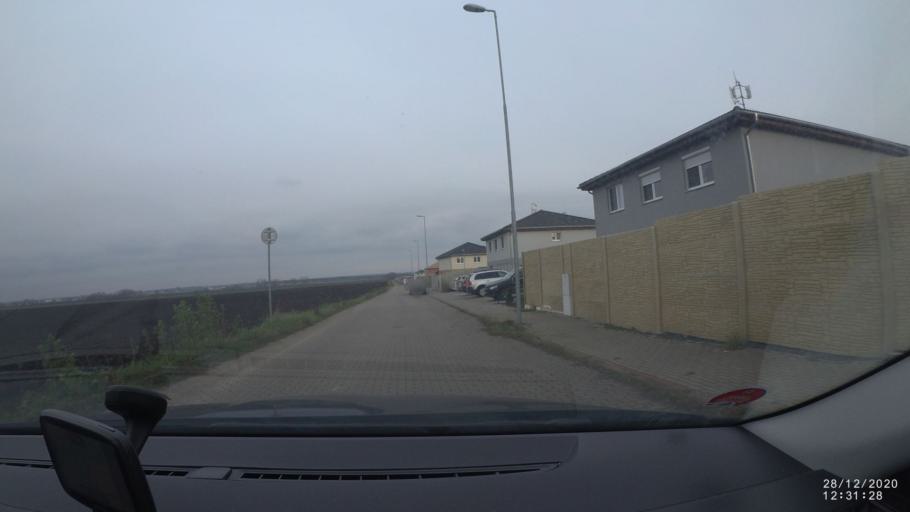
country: CZ
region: Central Bohemia
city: Kostelec nad Labem
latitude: 50.2025
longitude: 14.5900
